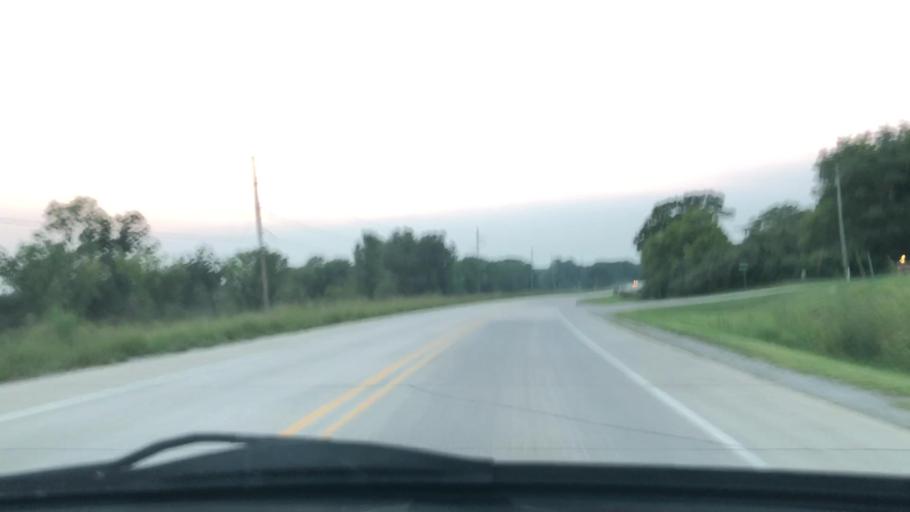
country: US
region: Iowa
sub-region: Johnson County
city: North Liberty
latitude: 41.8116
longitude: -91.6612
